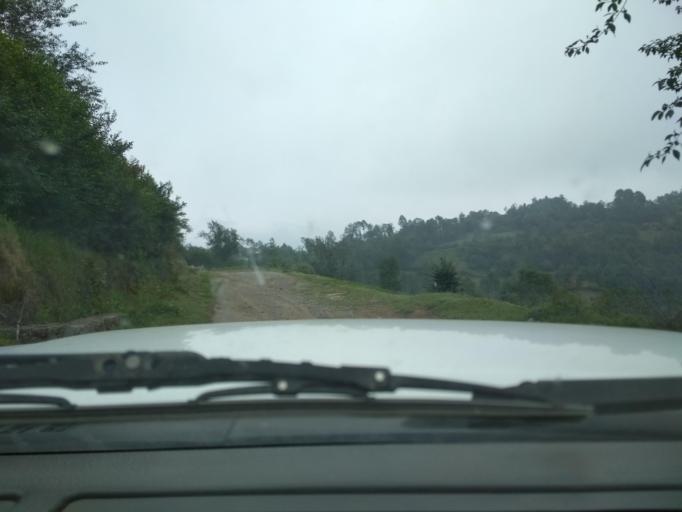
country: MX
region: Veracruz
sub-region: La Perla
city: Chilapa
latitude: 18.9941
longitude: -97.1669
